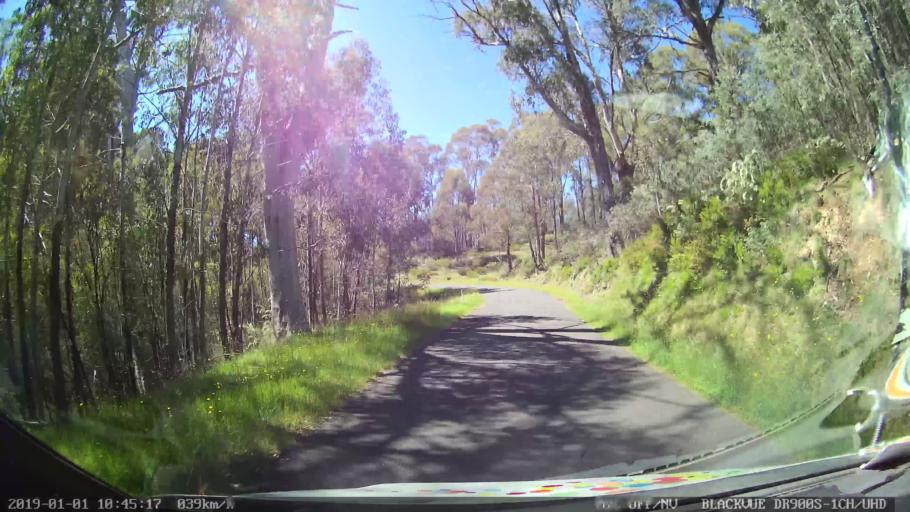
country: AU
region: New South Wales
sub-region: Snowy River
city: Jindabyne
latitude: -36.0351
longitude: 148.3369
